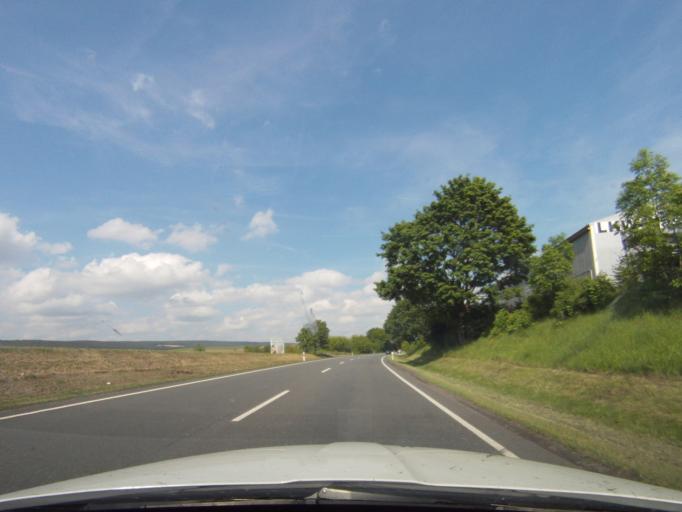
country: DE
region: Thuringia
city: Oppurg
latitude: 50.7135
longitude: 11.6617
